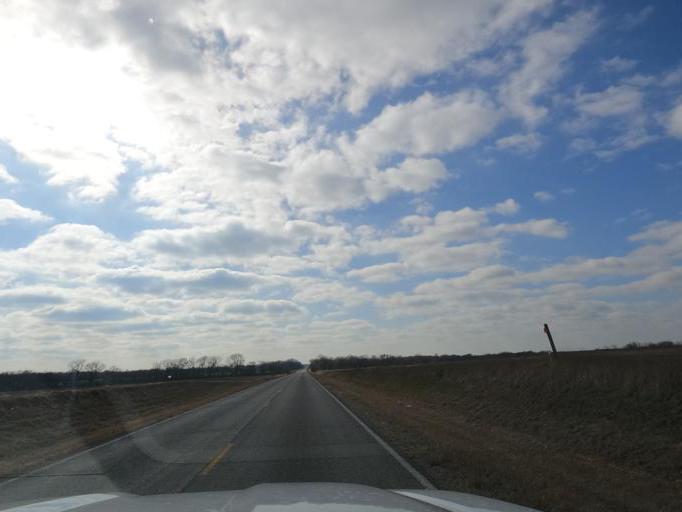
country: US
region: Kansas
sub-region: McPherson County
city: Inman
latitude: 38.2321
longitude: -97.8696
